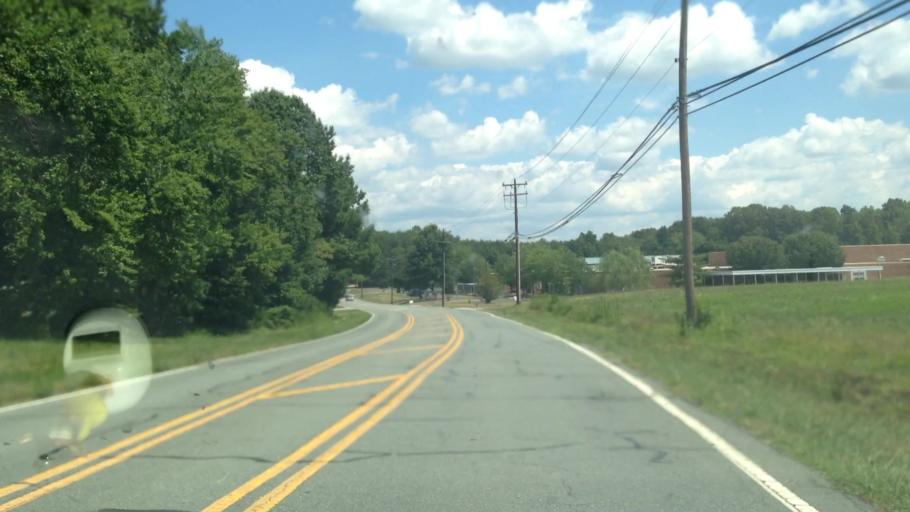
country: US
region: North Carolina
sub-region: Forsyth County
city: Kernersville
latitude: 36.1580
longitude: -80.0562
